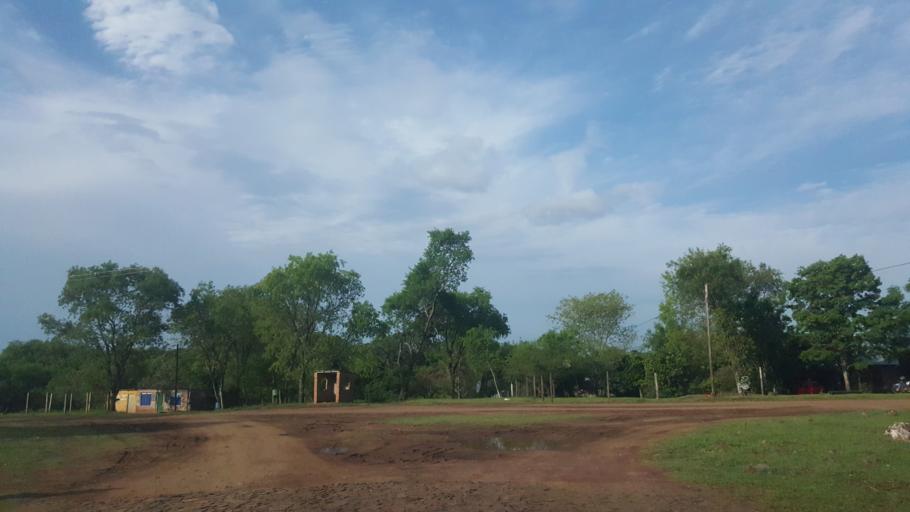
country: AR
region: Misiones
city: Cerro Cora
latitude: -27.5588
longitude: -55.7056
